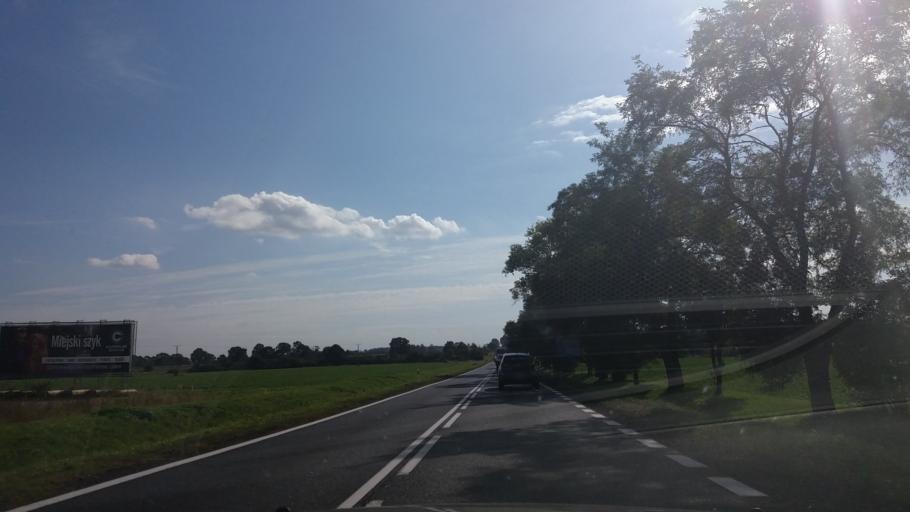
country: PL
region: Lower Silesian Voivodeship
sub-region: Powiat lubinski
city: Osiek
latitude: 51.3378
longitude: 16.2947
